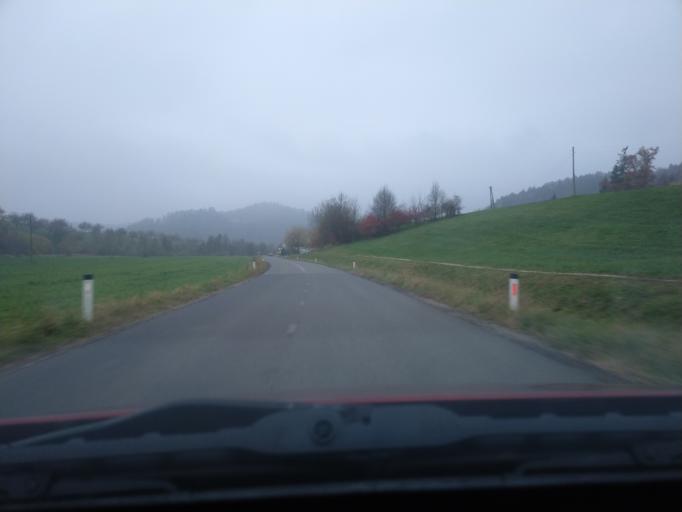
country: SI
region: Kungota
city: Zgornja Kungota
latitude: 46.6453
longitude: 15.6134
